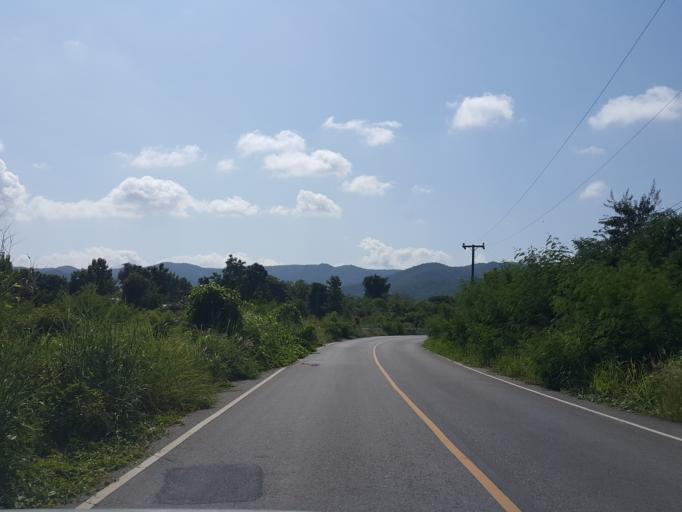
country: TH
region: Chiang Mai
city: Mae On
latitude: 18.7912
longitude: 99.1838
